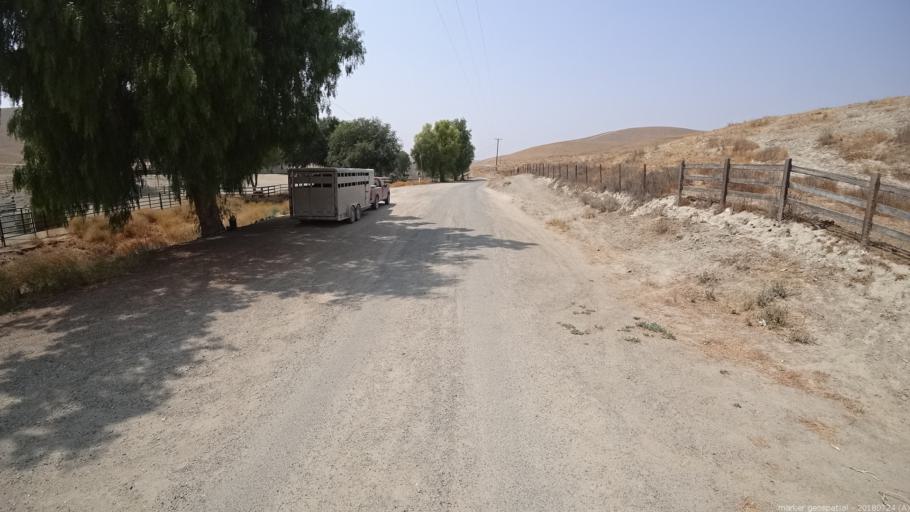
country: US
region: California
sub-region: Monterey County
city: King City
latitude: 36.1921
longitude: -120.9610
